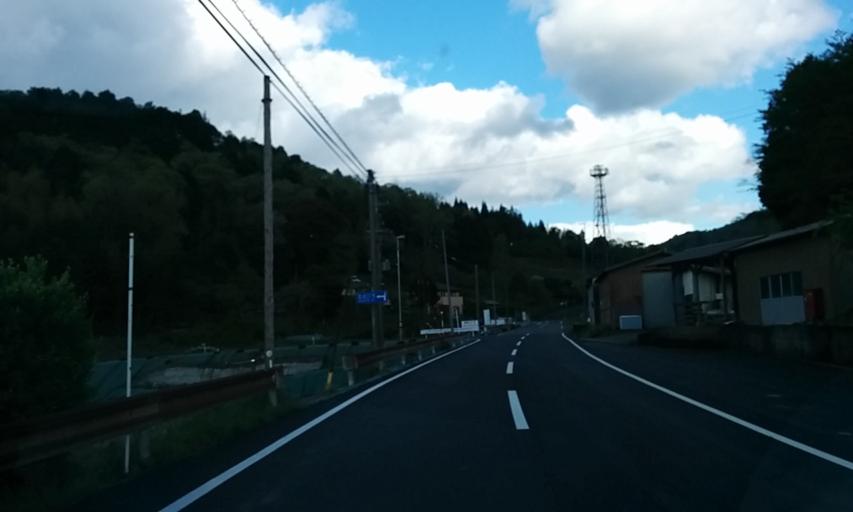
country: JP
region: Kyoto
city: Ayabe
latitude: 35.2718
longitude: 135.3597
